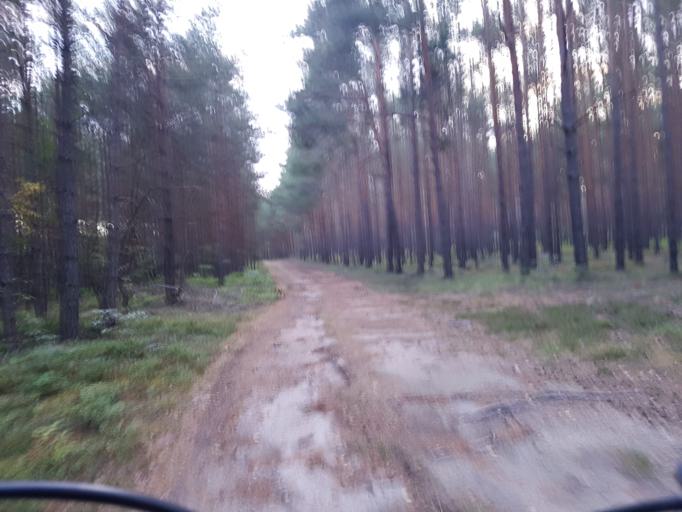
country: DE
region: Brandenburg
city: Trobitz
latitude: 51.5627
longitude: 13.4506
